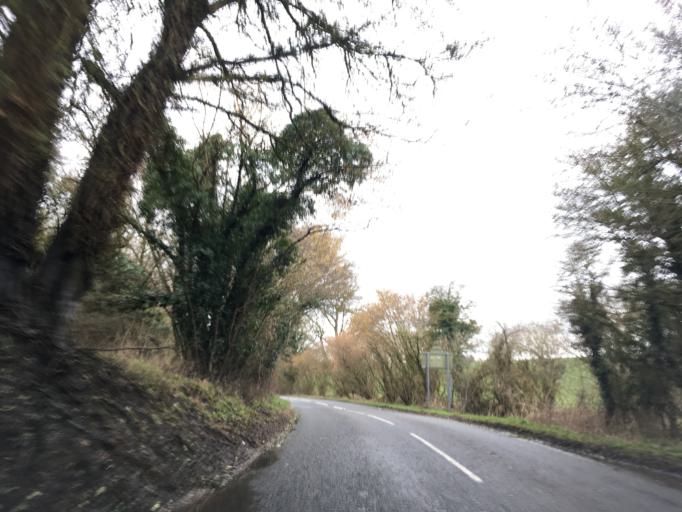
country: GB
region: England
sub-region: Wiltshire
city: Chilton Foliat
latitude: 51.4559
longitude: -1.5289
